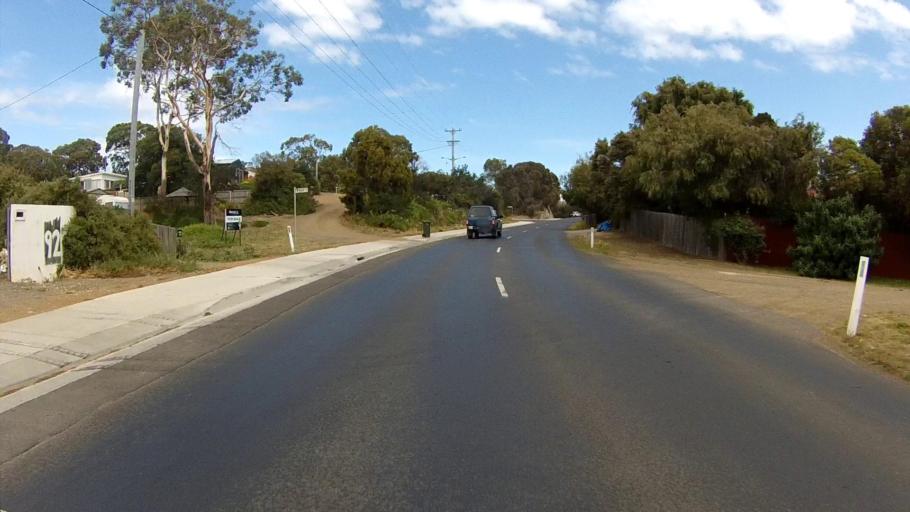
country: AU
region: Tasmania
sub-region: Sorell
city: Sorell
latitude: -42.8612
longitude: 147.6126
